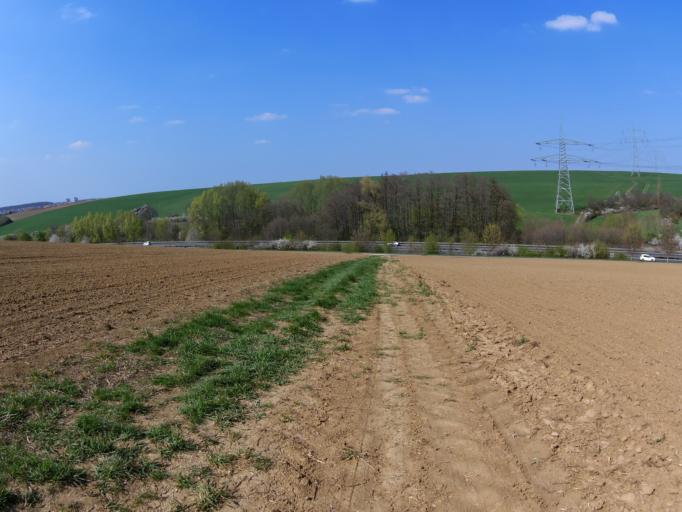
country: DE
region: Bavaria
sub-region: Regierungsbezirk Unterfranken
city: Rottendorf
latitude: 49.7814
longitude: 10.0464
